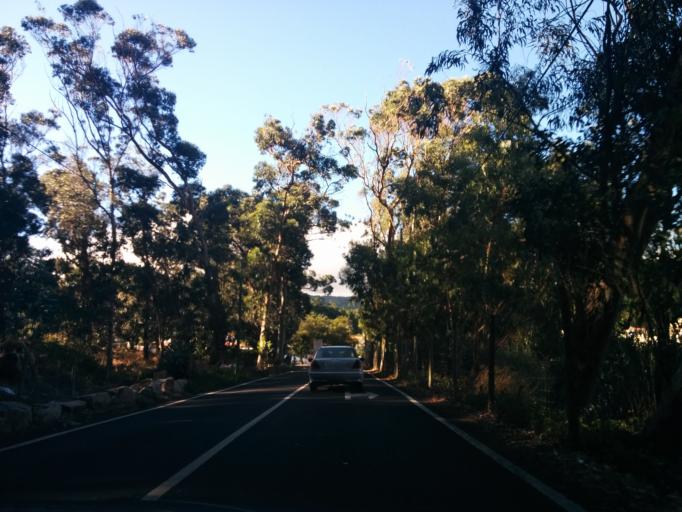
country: PT
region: Lisbon
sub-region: Cascais
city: Alcabideche
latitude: 38.7516
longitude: -9.4503
